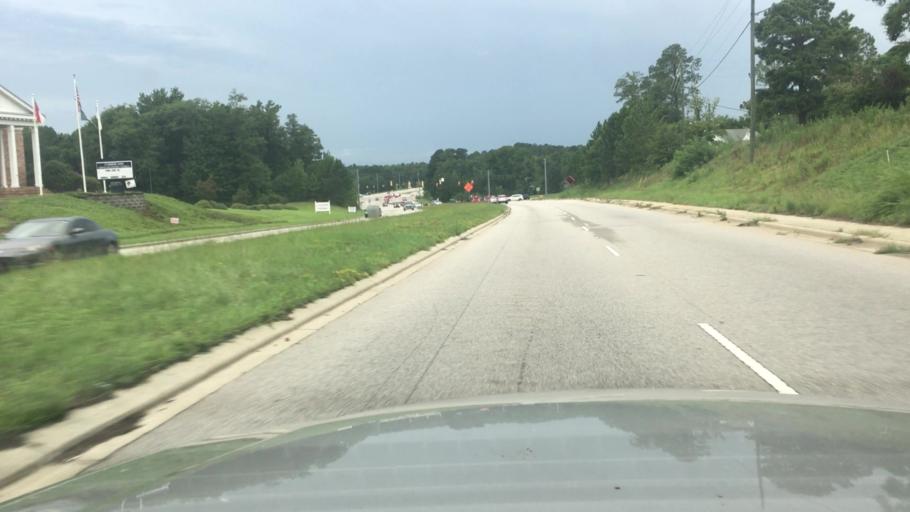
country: US
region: North Carolina
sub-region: Cumberland County
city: Hope Mills
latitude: 35.0001
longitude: -78.9741
